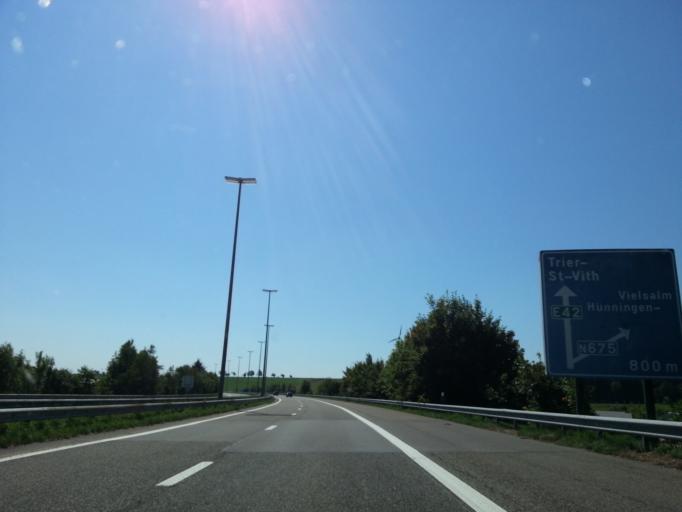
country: BE
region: Wallonia
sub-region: Province de Liege
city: Saint-Vith
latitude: 50.2986
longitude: 6.0811
